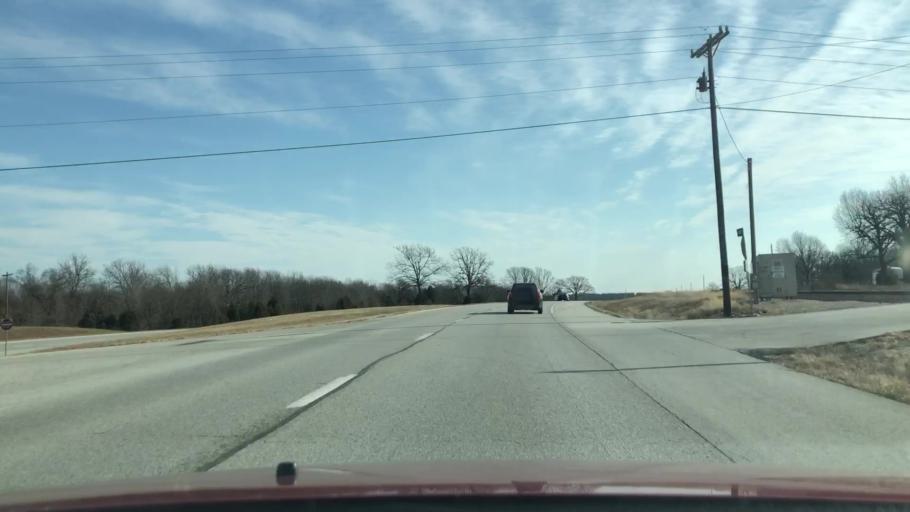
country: US
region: Missouri
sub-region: Webster County
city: Seymour
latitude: 37.1307
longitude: -92.7199
